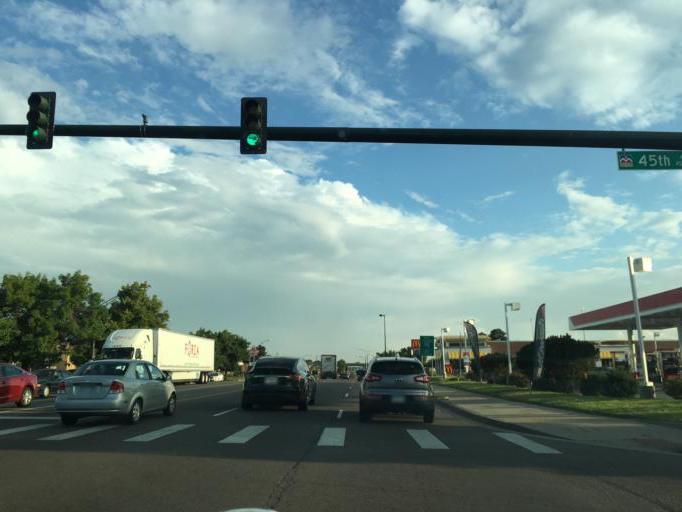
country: US
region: Colorado
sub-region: Adams County
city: Aurora
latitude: 39.7781
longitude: -104.8471
